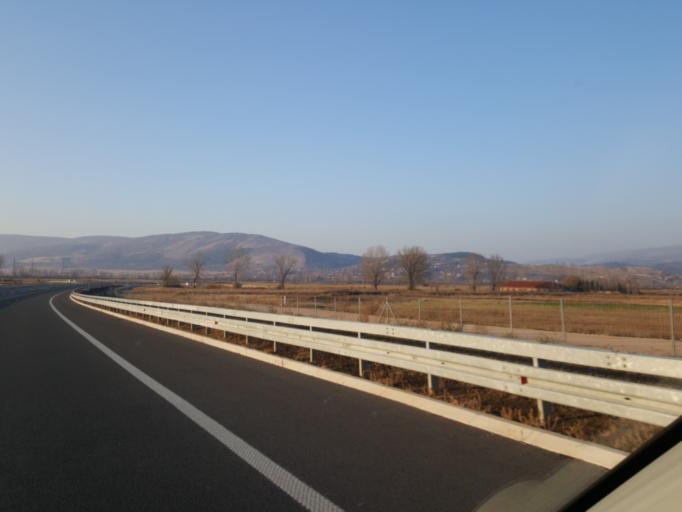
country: RS
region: Central Serbia
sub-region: Pirotski Okrug
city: Pirot
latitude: 43.1314
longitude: 22.5752
